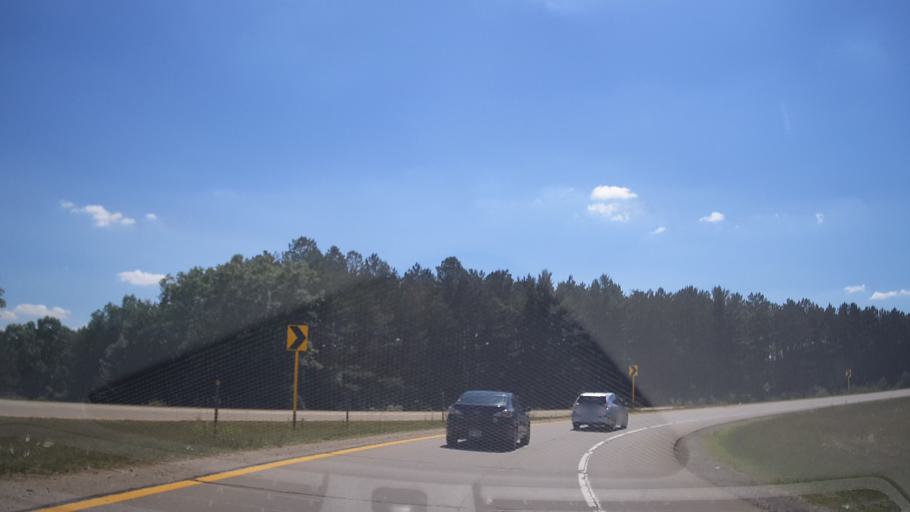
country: US
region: Michigan
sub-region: Clare County
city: Clare
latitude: 43.8633
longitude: -84.9094
